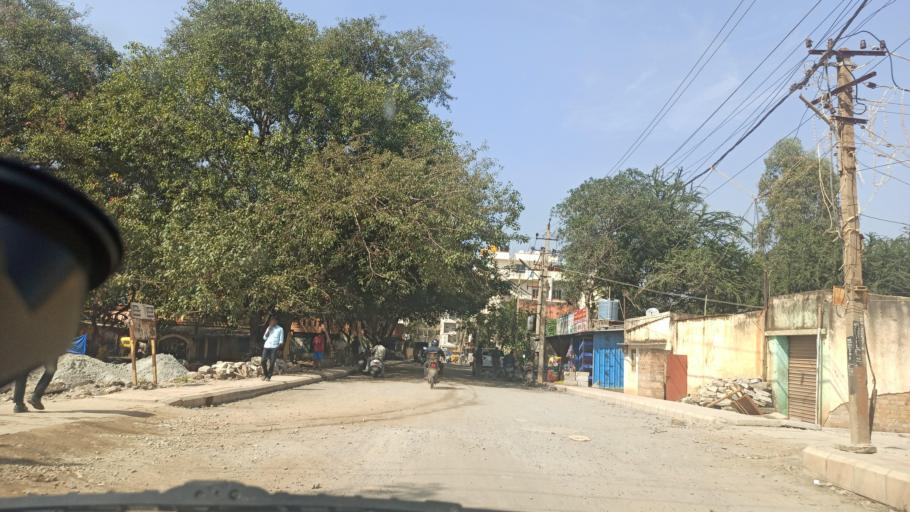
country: IN
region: Karnataka
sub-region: Bangalore Urban
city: Bangalore
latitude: 12.9262
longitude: 77.6912
